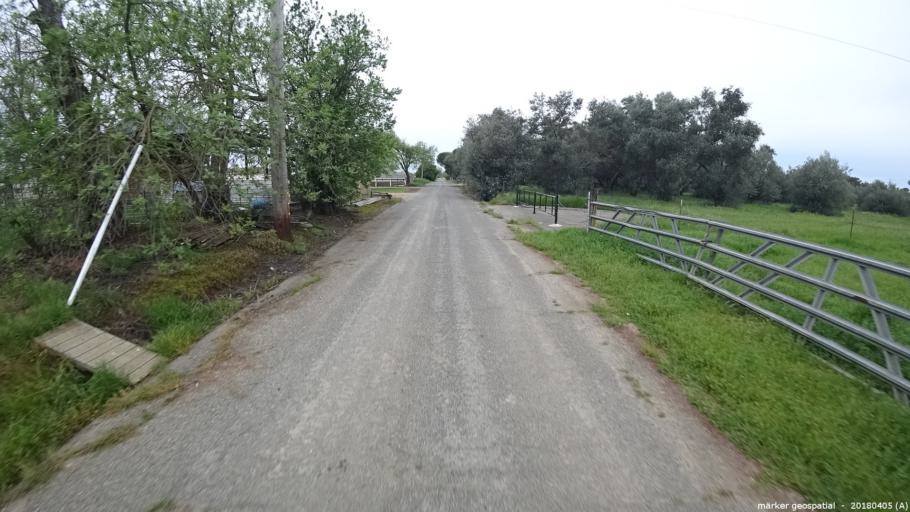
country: US
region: California
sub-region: Sacramento County
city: Herald
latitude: 38.2959
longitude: -121.2217
